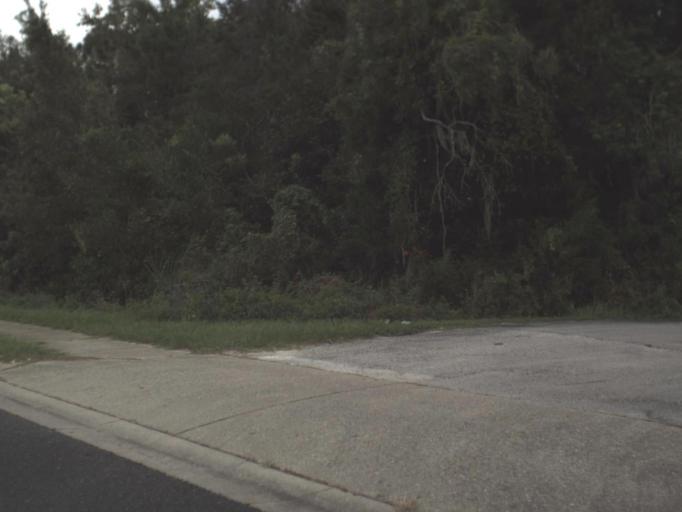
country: US
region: Florida
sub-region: Citrus County
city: Inverness Highlands North
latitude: 28.8444
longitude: -82.3665
